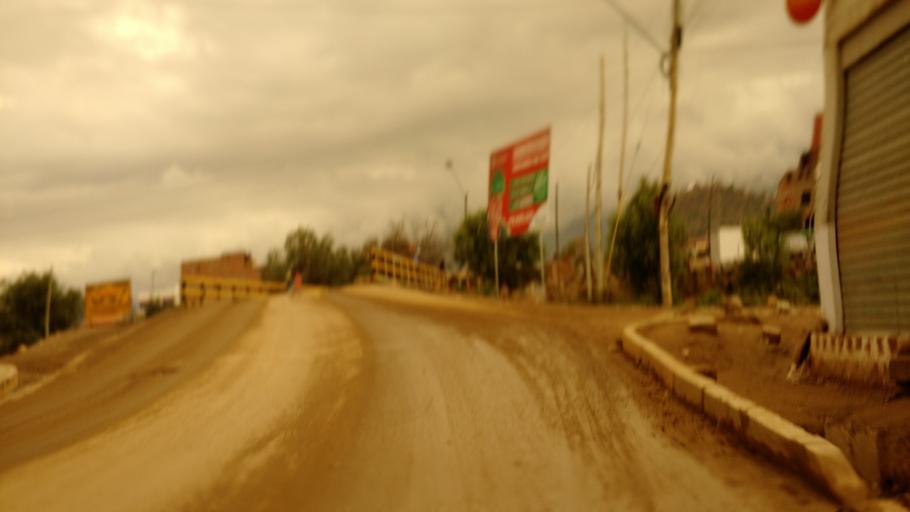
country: BO
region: Cochabamba
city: Cochabamba
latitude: -17.4430
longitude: -66.1553
